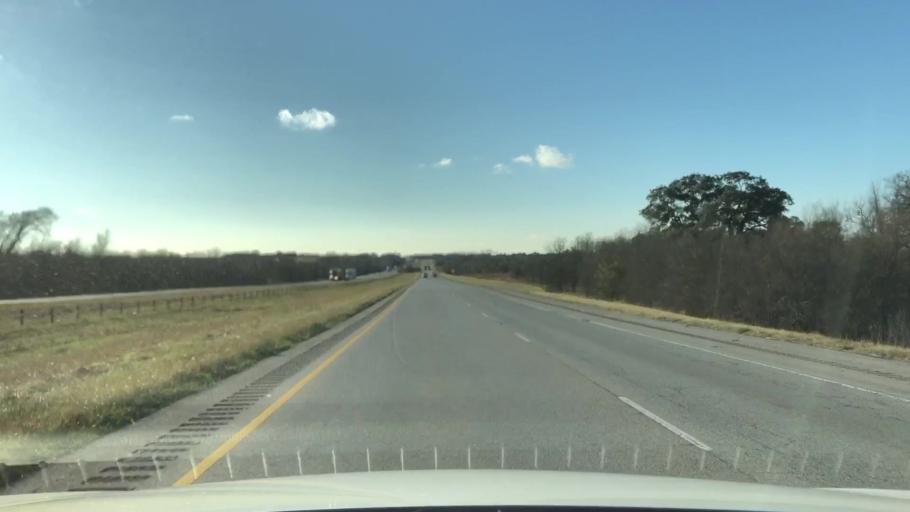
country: US
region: Texas
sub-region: Fayette County
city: Schulenburg
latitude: 29.6965
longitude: -96.8645
